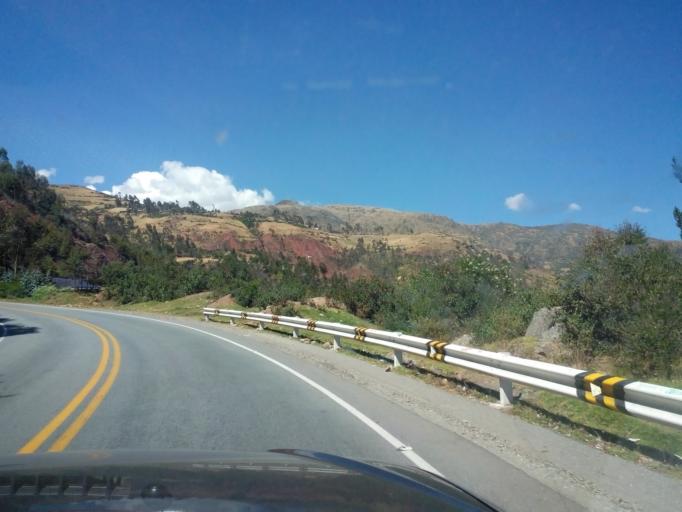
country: PE
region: Cusco
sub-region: Provincia de Anta
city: Limatambo
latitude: -13.4480
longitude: -72.4001
